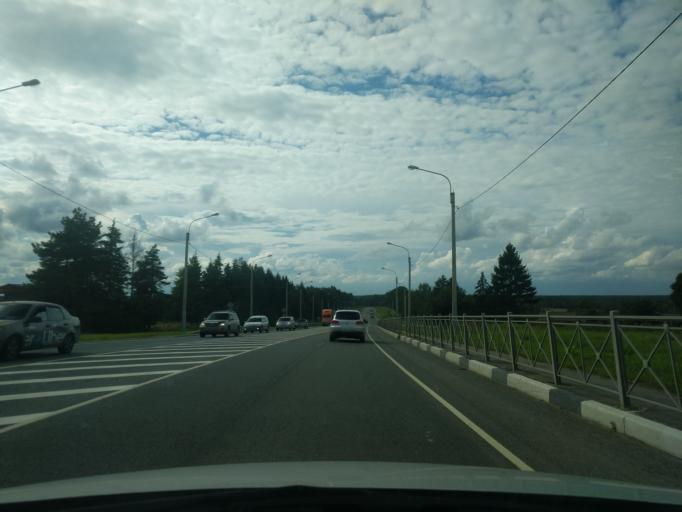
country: RU
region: Jaroslavl
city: Levashevo
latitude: 57.6429
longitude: 40.5248
